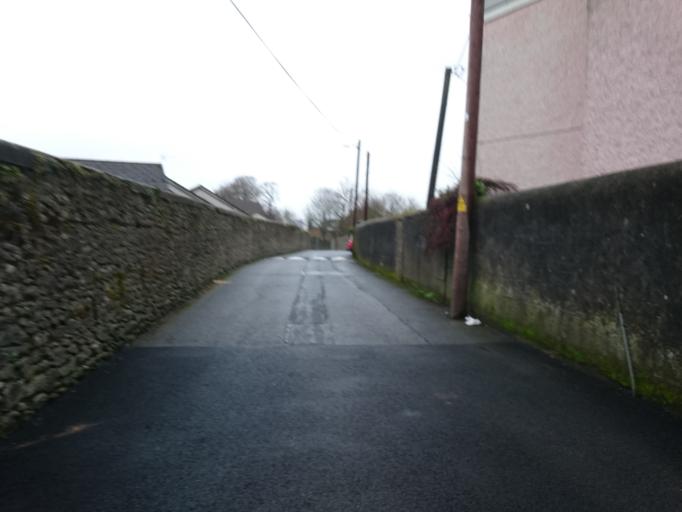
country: IE
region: Leinster
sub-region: Kilkenny
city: Kilkenny
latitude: 52.6572
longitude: -7.2593
